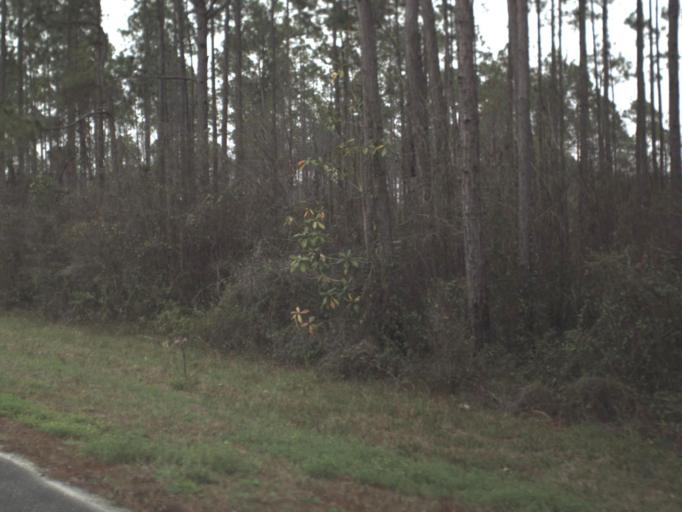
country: US
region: Florida
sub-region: Franklin County
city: Eastpoint
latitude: 29.8263
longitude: -84.8993
